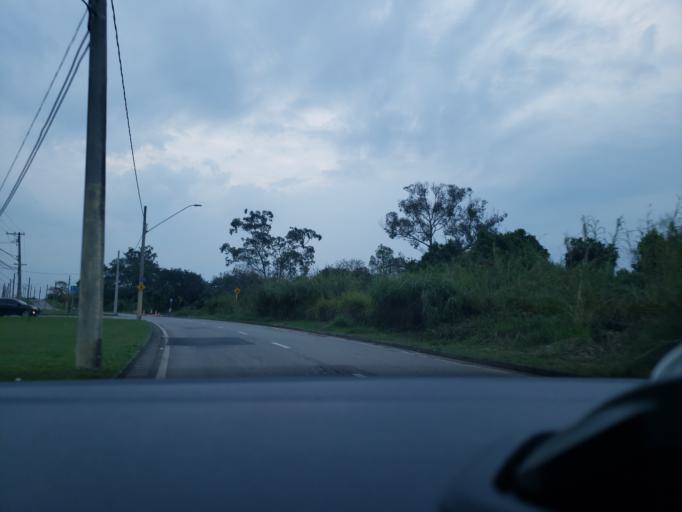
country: BR
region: Sao Paulo
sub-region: Sao Jose Dos Campos
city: Sao Jose dos Campos
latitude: -23.1965
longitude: -45.9476
